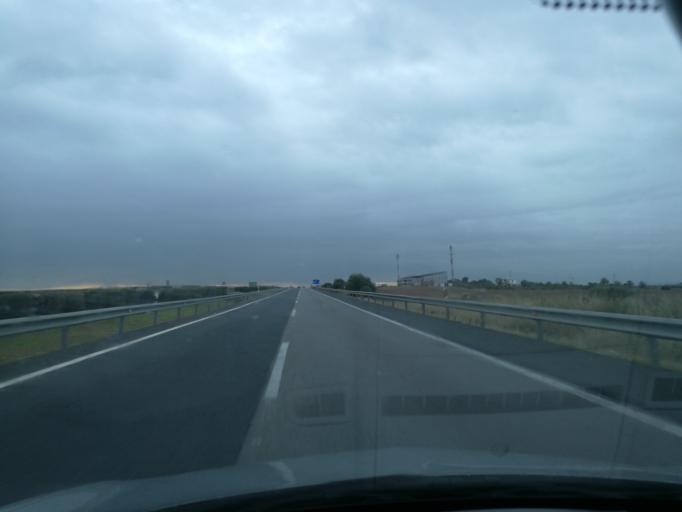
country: ES
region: Andalusia
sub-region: Provincia de Sevilla
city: Carmona
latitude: 37.4670
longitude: -5.7195
